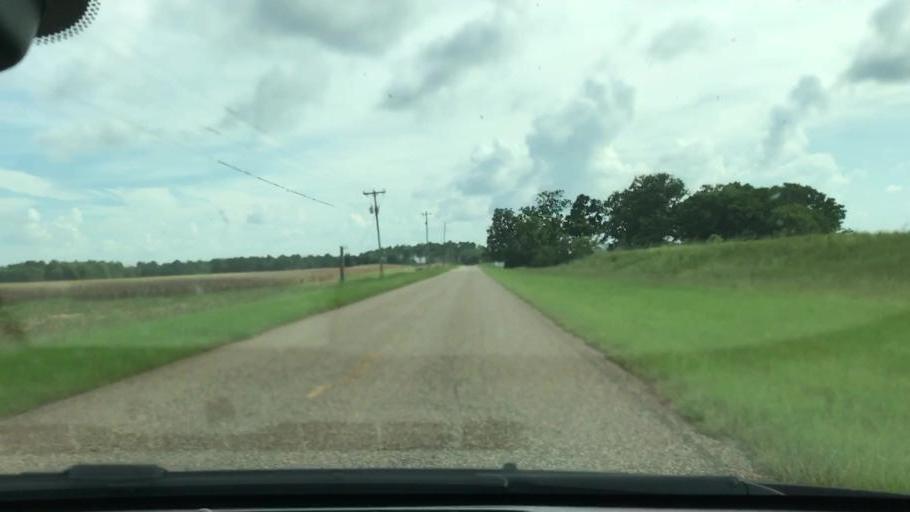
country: US
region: Georgia
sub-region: Clay County
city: Fort Gaines
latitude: 31.5237
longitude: -84.9545
